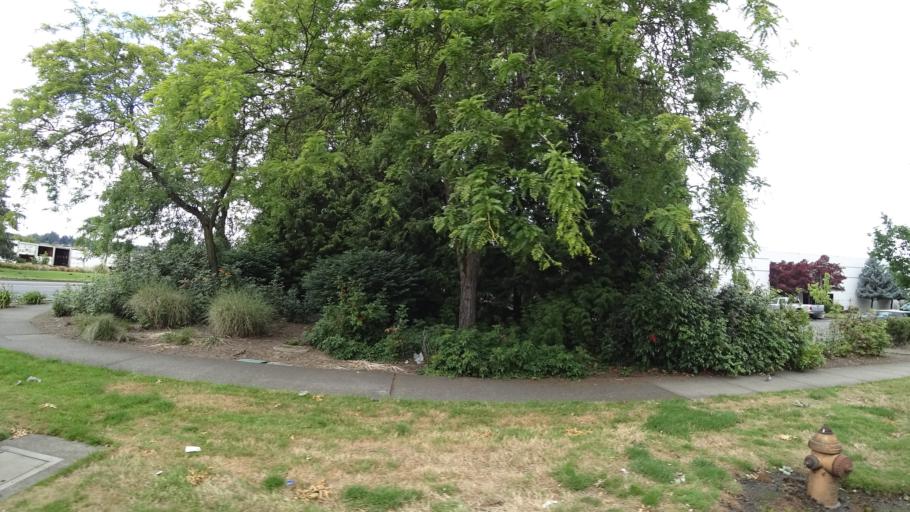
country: US
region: Oregon
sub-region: Multnomah County
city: Portland
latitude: 45.5660
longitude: -122.7087
